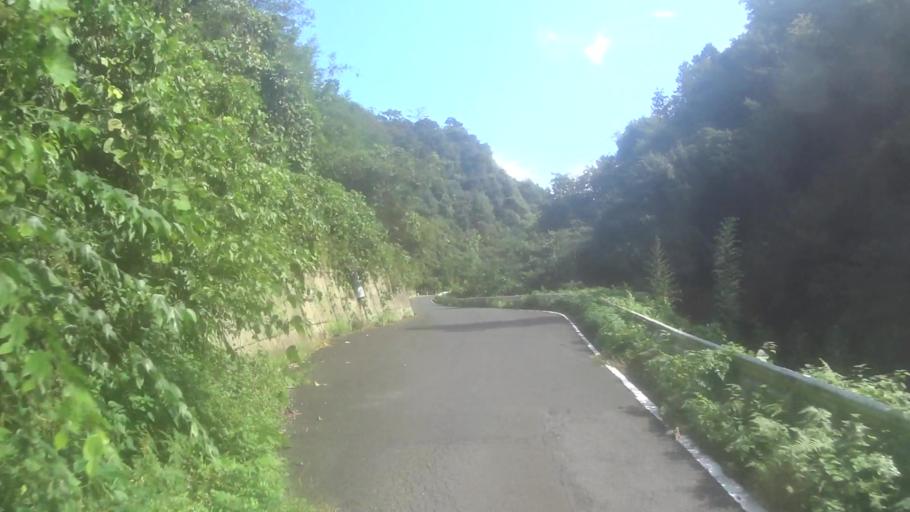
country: JP
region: Kyoto
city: Miyazu
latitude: 35.6100
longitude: 135.1125
